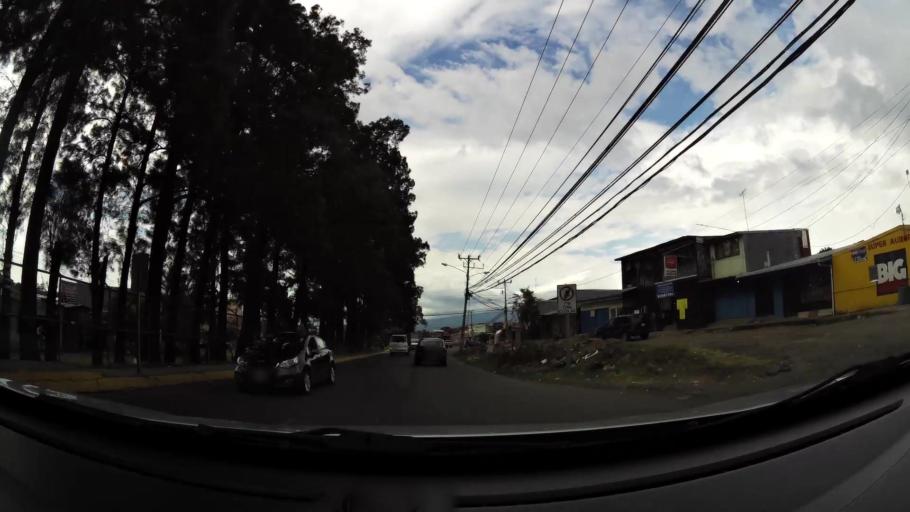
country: CR
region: San Jose
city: San Felipe
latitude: 9.9197
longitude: -84.1178
